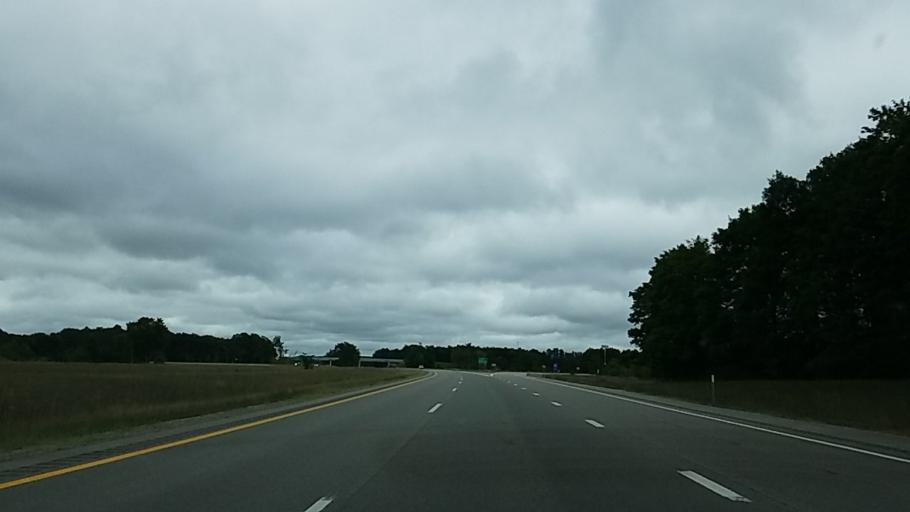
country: US
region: Michigan
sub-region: Otsego County
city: Gaylord
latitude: 45.1546
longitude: -84.6690
